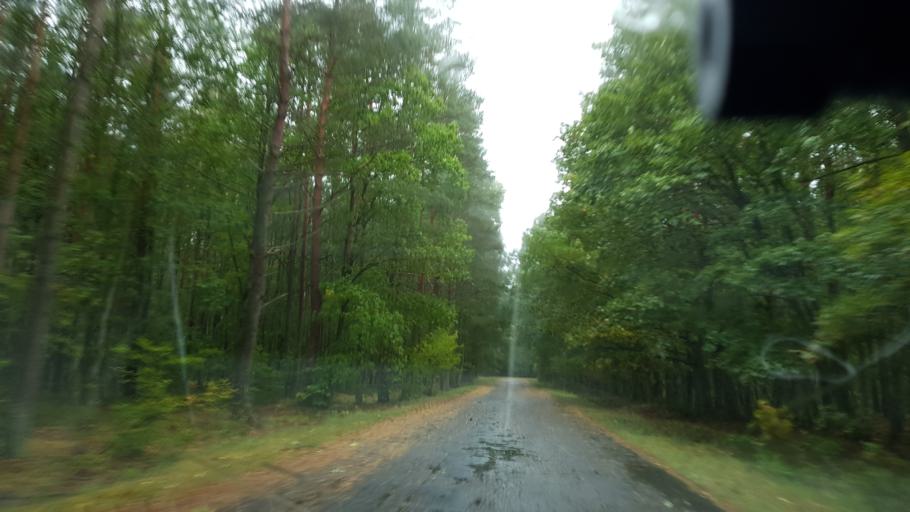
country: PL
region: West Pomeranian Voivodeship
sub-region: Powiat goleniowski
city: Przybiernow
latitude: 53.7017
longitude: 14.7183
